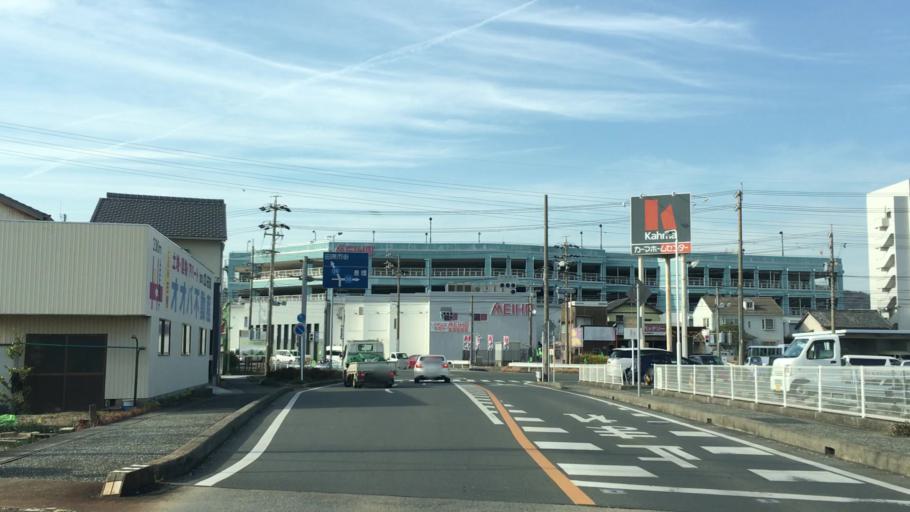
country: JP
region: Aichi
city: Tahara
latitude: 34.6671
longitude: 137.2746
